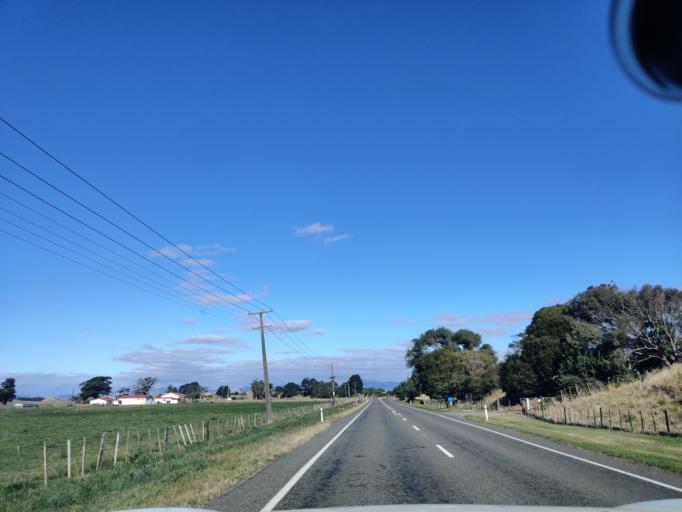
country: NZ
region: Manawatu-Wanganui
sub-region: Horowhenua District
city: Foxton
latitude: -40.4063
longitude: 175.3740
